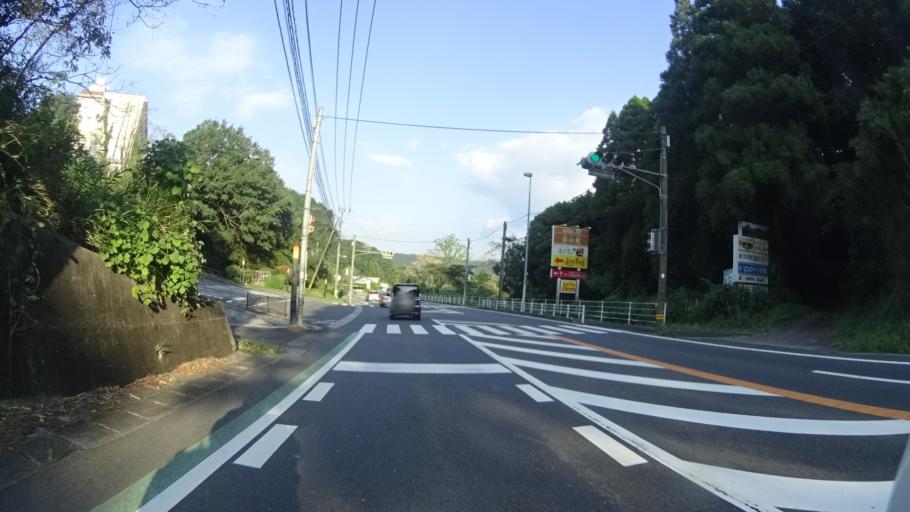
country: JP
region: Oita
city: Bungo-Takada-shi
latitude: 33.4432
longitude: 131.3471
